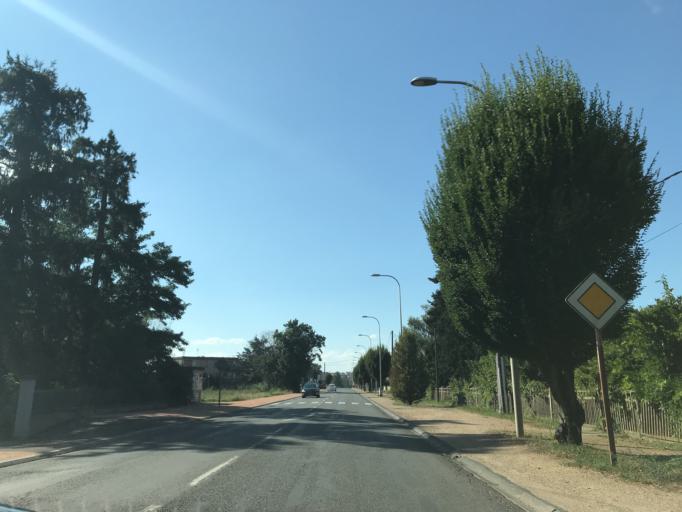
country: FR
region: Auvergne
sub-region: Departement du Puy-de-Dome
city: Pont-du-Chateau
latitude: 45.7894
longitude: 3.2651
